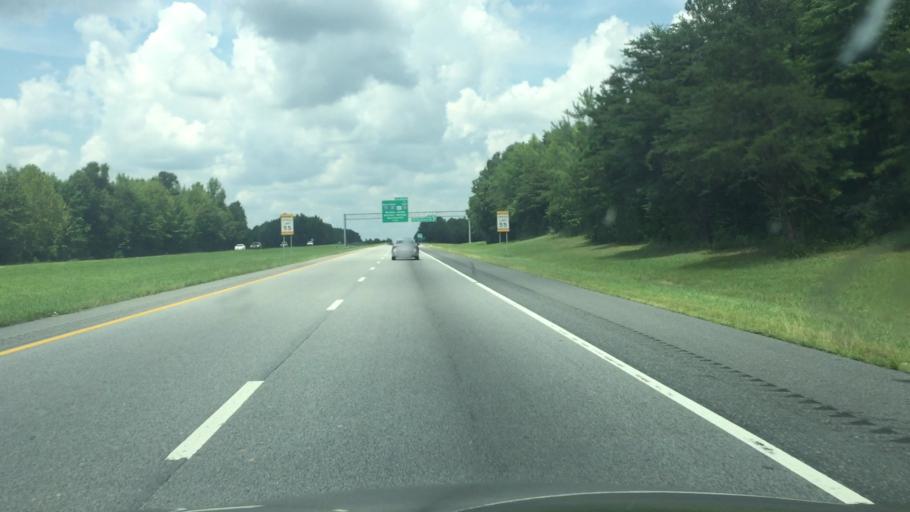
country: US
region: North Carolina
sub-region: Guilford County
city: Pleasant Garden
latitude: 35.9814
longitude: -79.8231
